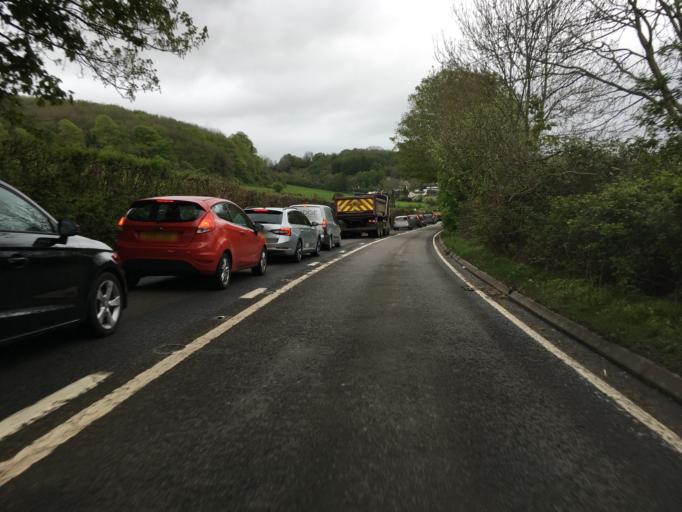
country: GB
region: England
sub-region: North Somerset
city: Banwell
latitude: 51.3290
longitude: -2.8555
